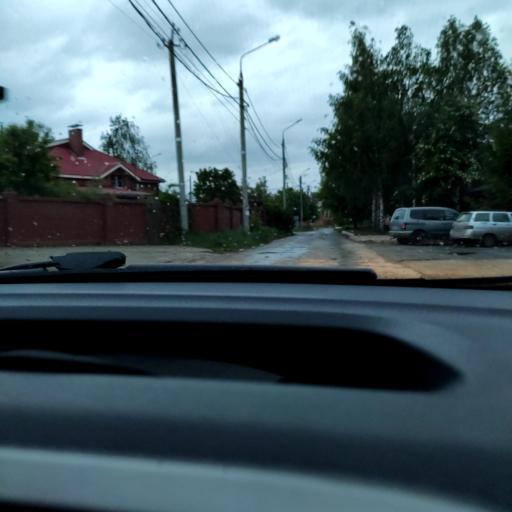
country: RU
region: Samara
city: Tol'yatti
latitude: 53.5427
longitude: 49.3738
